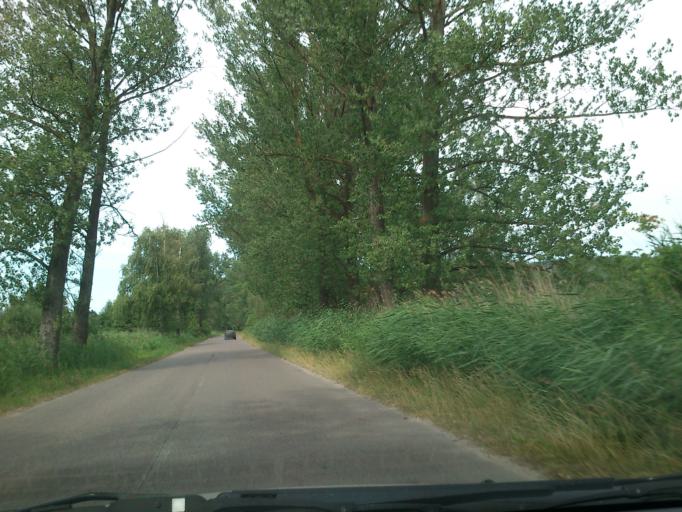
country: PL
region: West Pomeranian Voivodeship
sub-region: Powiat kamienski
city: Miedzyzdroje
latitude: 53.8817
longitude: 14.4330
